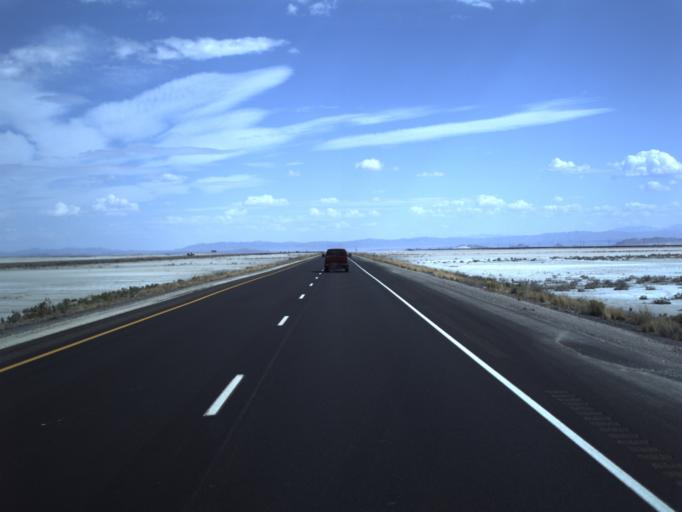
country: US
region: Utah
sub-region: Tooele County
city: Wendover
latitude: 40.7304
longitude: -113.4800
